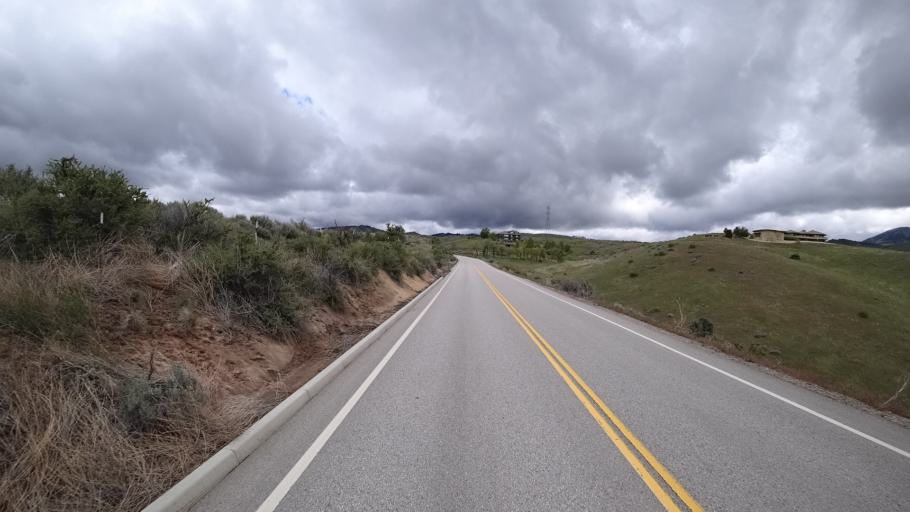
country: US
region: Idaho
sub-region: Ada County
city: Boise
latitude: 43.6953
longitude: -116.1706
